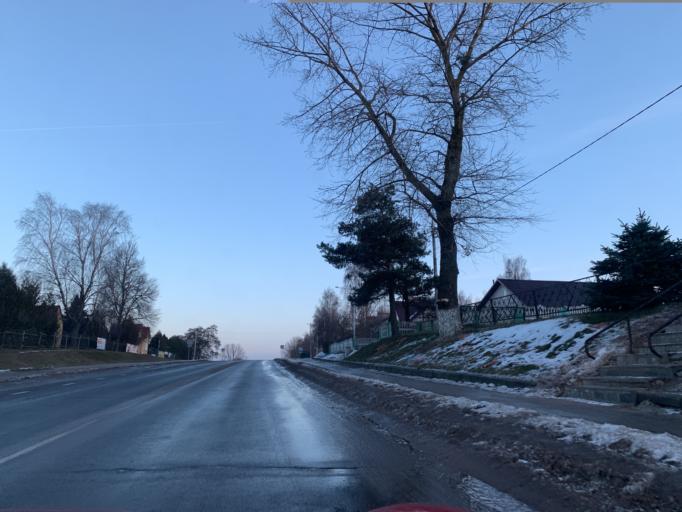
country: BY
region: Minsk
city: Nyasvizh
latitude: 53.2326
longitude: 26.6528
